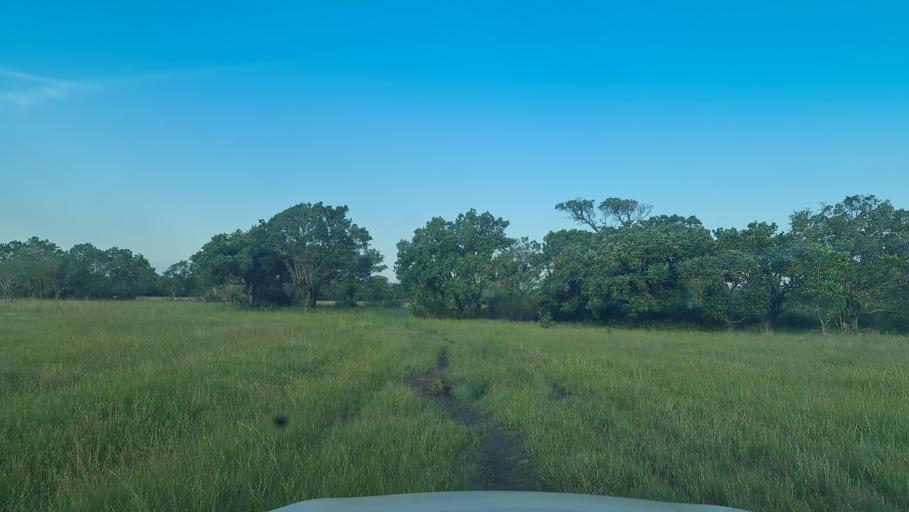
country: MZ
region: Gaza
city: Macia
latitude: -25.2220
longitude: 33.0302
